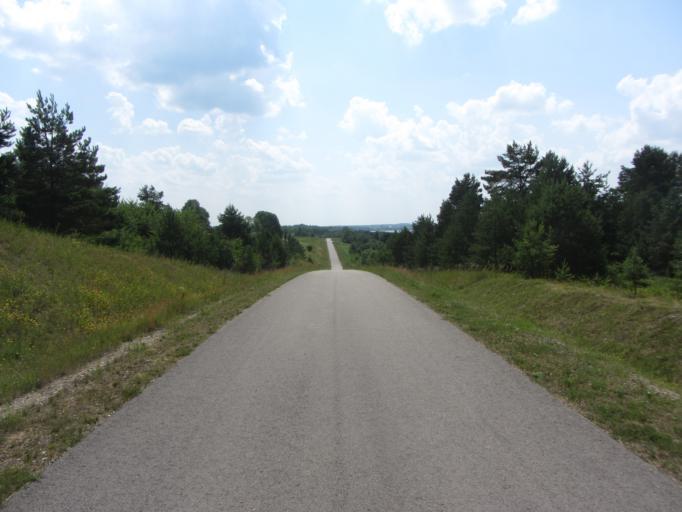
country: LT
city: Lazdijai
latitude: 54.1941
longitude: 23.4214
